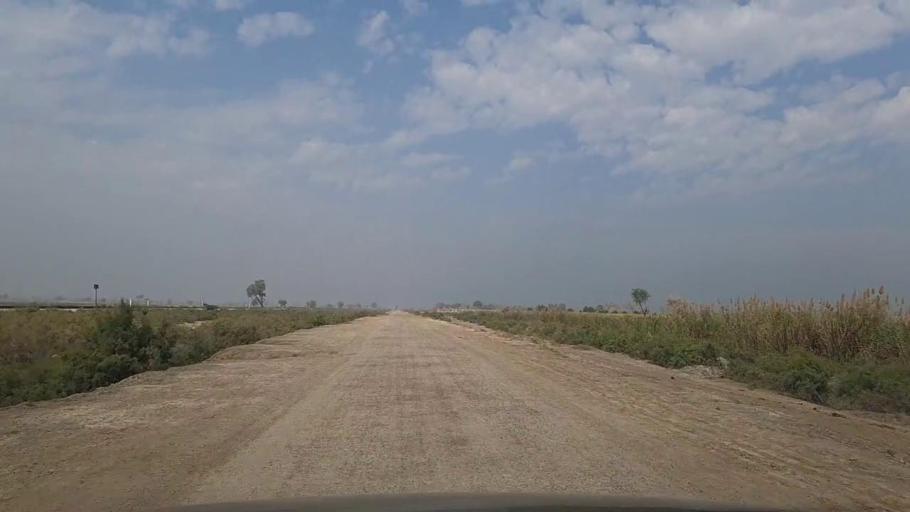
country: PK
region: Sindh
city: Daur
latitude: 26.3889
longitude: 68.3510
